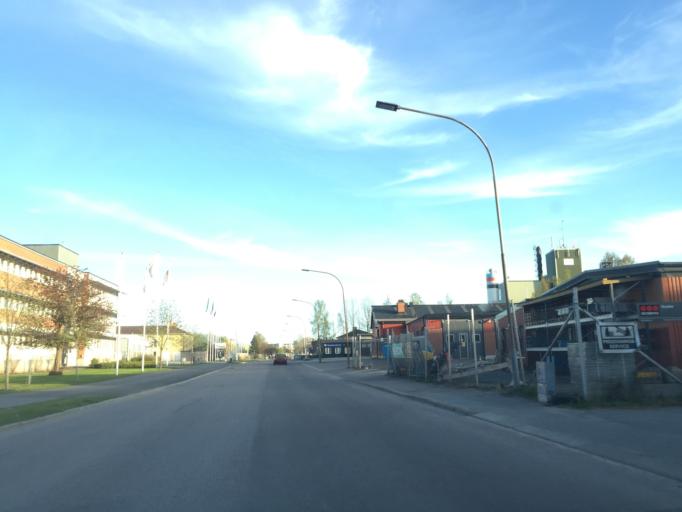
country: SE
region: OErebro
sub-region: Orebro Kommun
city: Orebro
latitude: 59.2927
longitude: 15.2092
